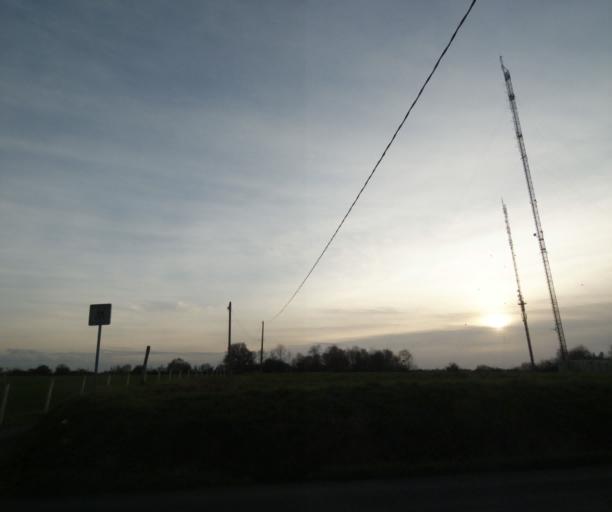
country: FR
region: Pays de la Loire
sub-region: Departement de la Sarthe
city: Rouillon
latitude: 48.0044
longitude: 0.1628
